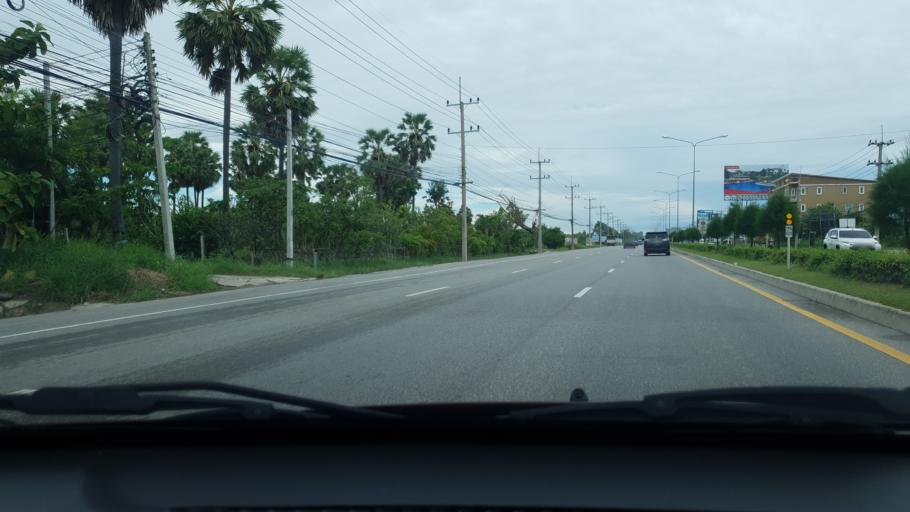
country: TH
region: Phetchaburi
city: Cha-am
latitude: 12.7547
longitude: 99.9618
